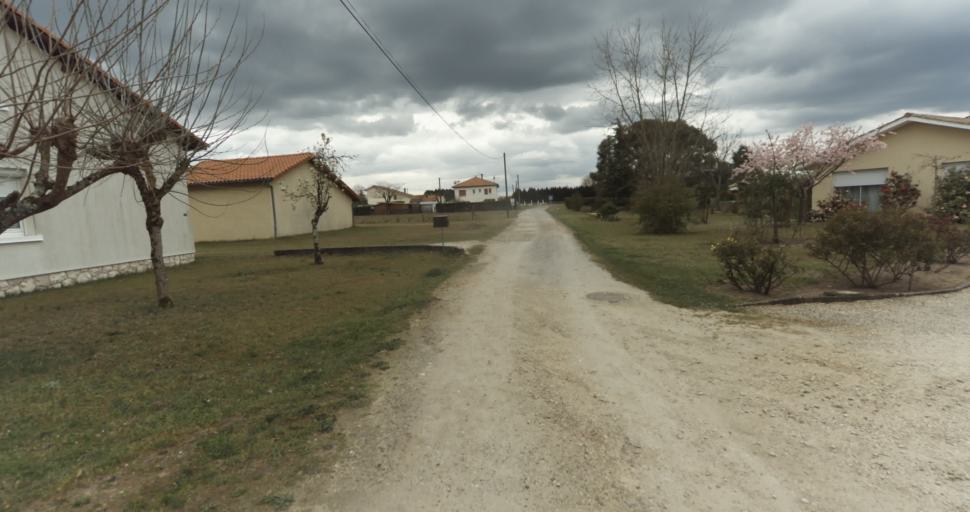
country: FR
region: Aquitaine
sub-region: Departement des Landes
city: Roquefort
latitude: 44.0261
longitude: -0.3314
